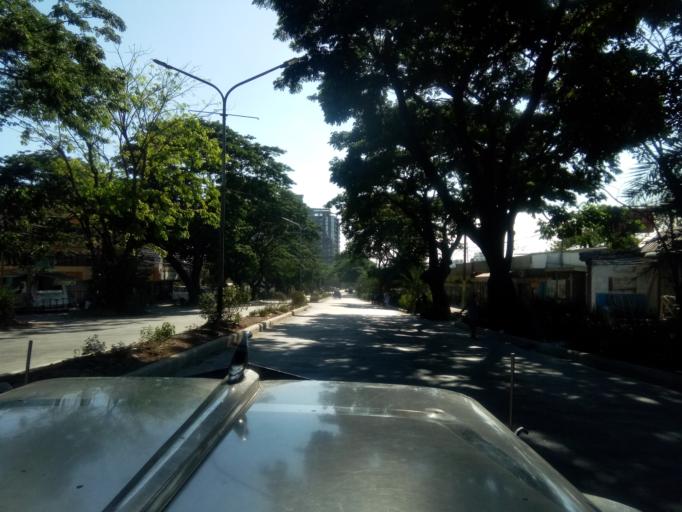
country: PH
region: Calabarzon
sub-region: Province of Cavite
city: Dasmarinas
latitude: 14.3271
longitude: 120.9491
